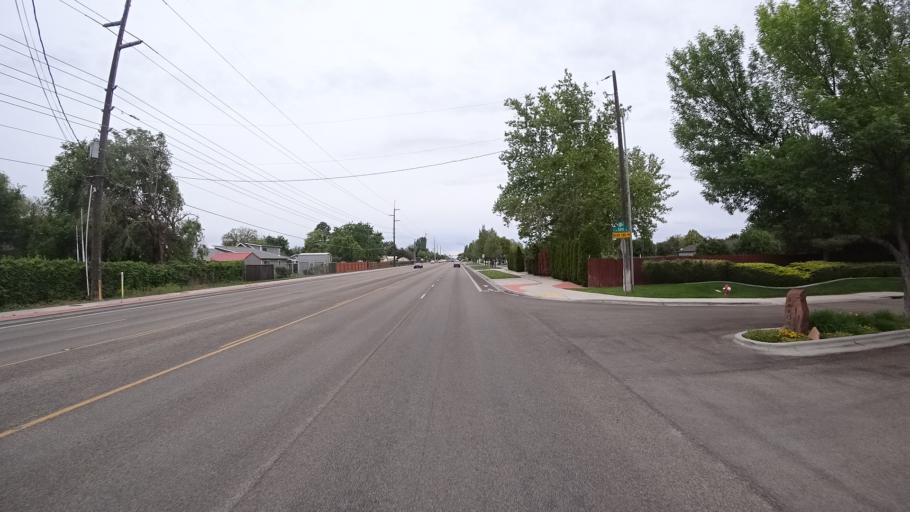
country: US
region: Idaho
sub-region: Ada County
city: Garden City
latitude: 43.6340
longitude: -116.3090
